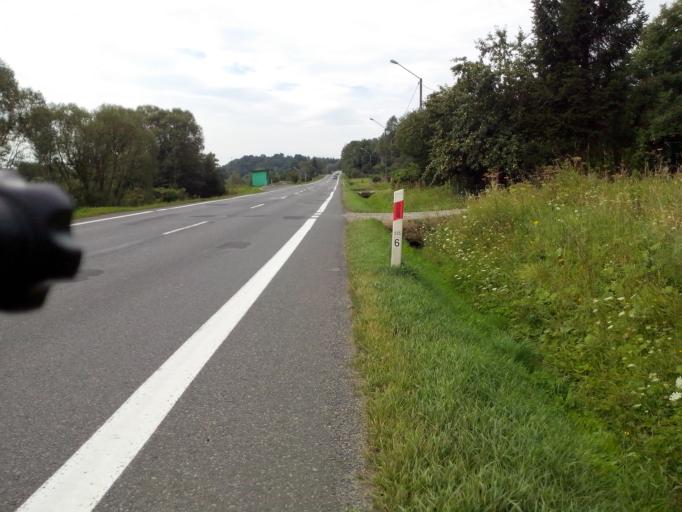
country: PL
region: Subcarpathian Voivodeship
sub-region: Powiat brzozowski
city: Domaradz
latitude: 49.7782
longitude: 21.9449
